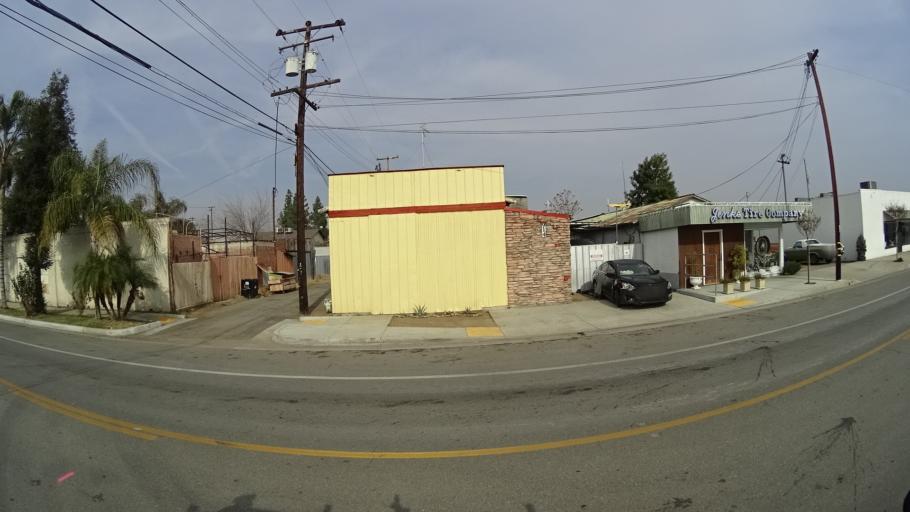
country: US
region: California
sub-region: Kern County
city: Bakersfield
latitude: 35.3781
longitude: -119.0124
